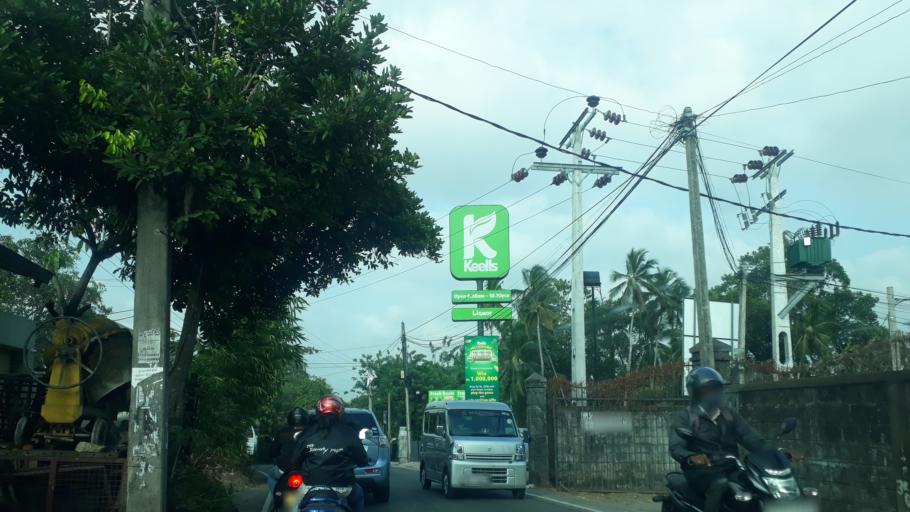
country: LK
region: Western
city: Battaramulla South
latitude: 6.8960
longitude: 79.9413
